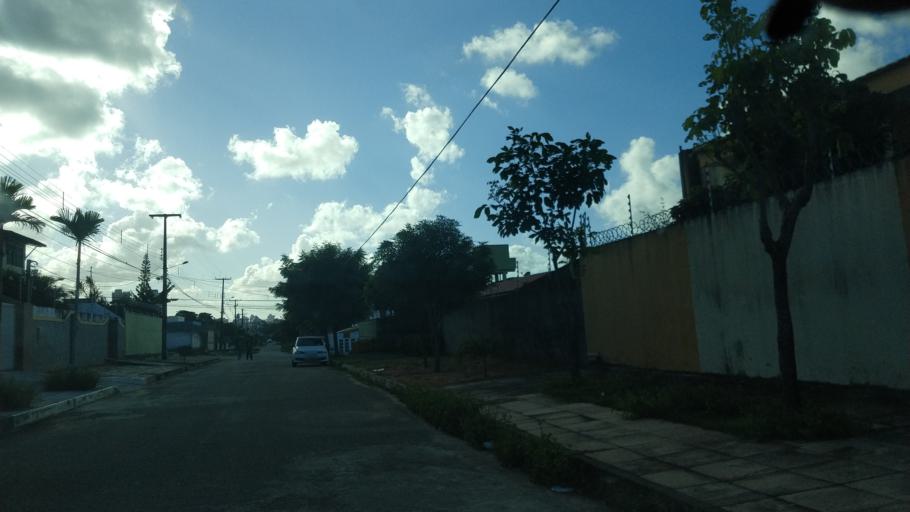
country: BR
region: Rio Grande do Norte
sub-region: Natal
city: Natal
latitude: -5.8481
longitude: -35.2021
